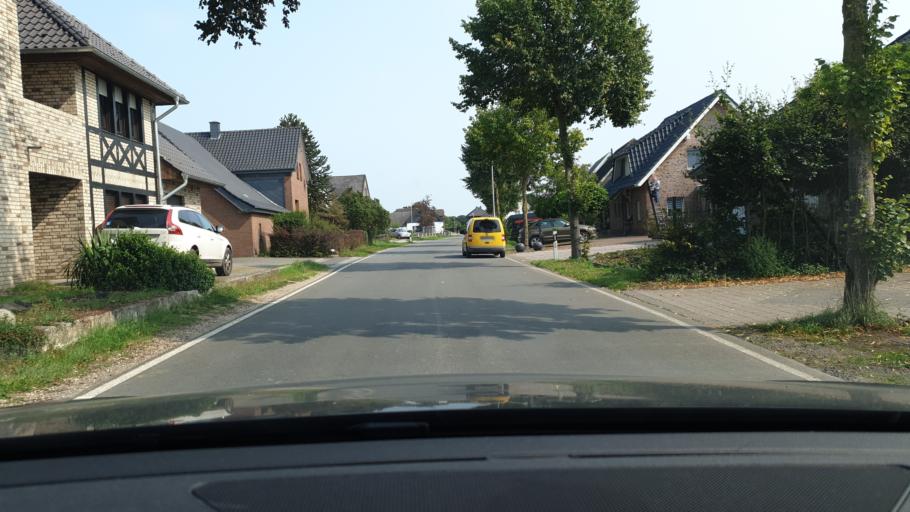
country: NL
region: Gelderland
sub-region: Gemeente Zevenaar
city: Zevenaar
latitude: 51.8482
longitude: 6.0701
